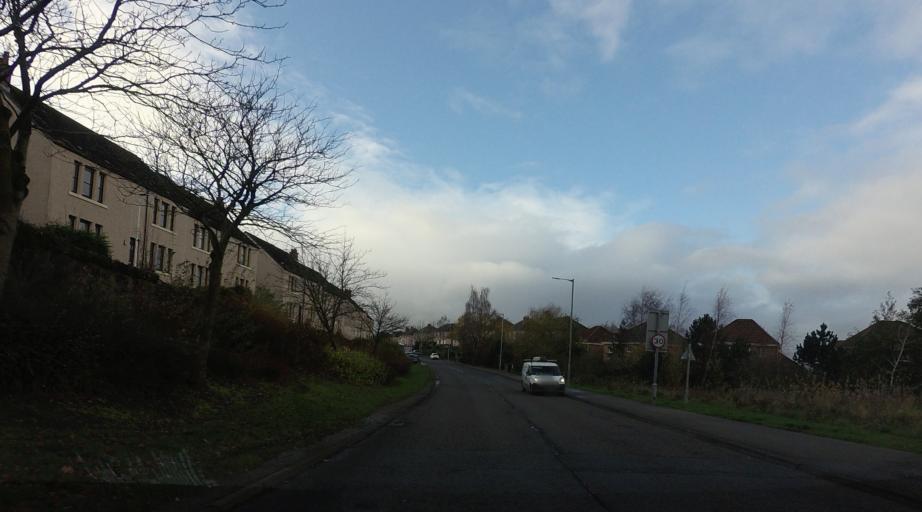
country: GB
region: Scotland
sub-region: Falkirk
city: Polmont
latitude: 55.9740
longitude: -3.7031
